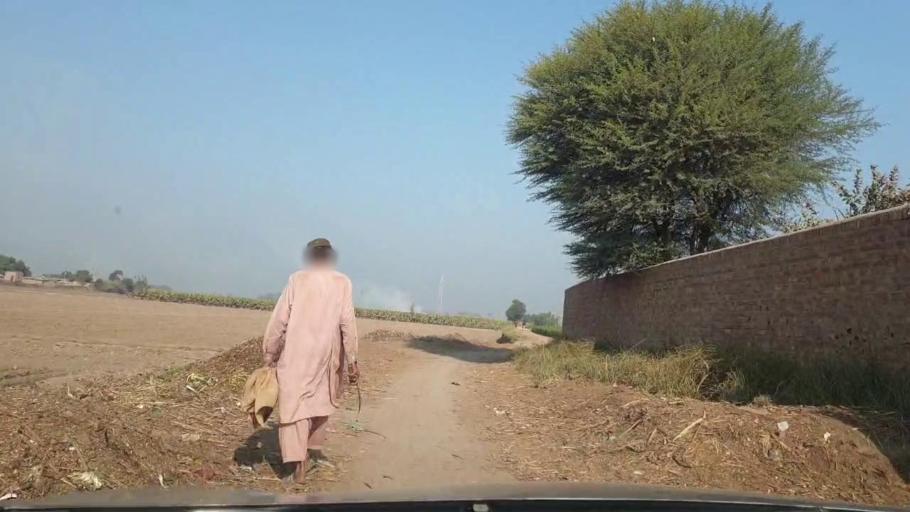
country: PK
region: Sindh
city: Tando Allahyar
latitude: 25.4872
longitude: 68.7420
